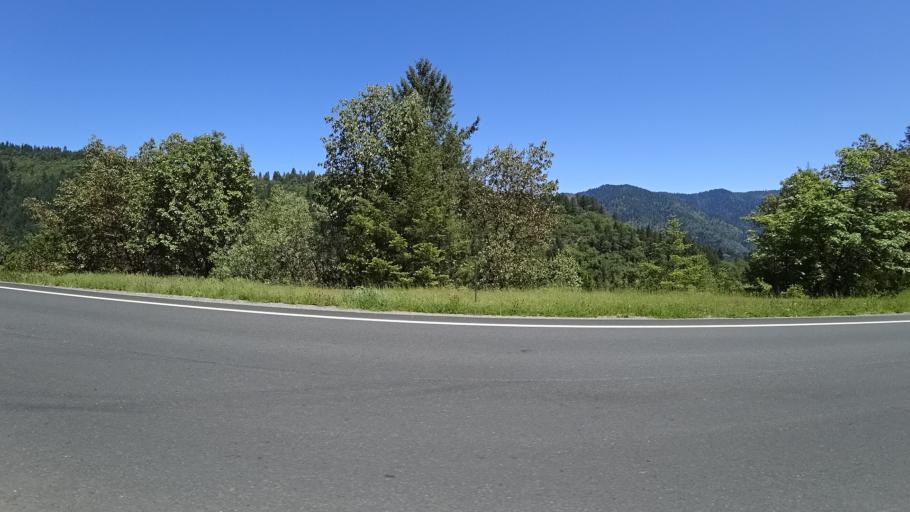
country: US
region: California
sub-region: Humboldt County
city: Willow Creek
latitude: 40.9459
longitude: -123.6503
